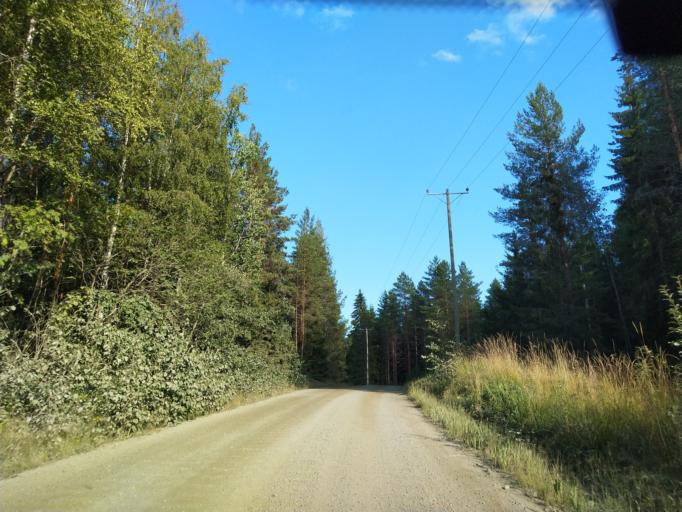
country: FI
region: Central Finland
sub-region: Jaemsae
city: Kuhmoinen
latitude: 61.6901
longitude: 24.9571
